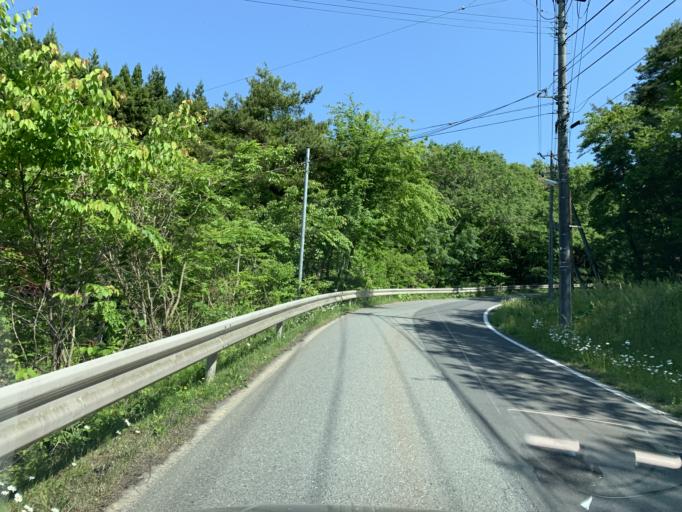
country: JP
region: Iwate
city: Mizusawa
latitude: 39.0465
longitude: 141.0658
